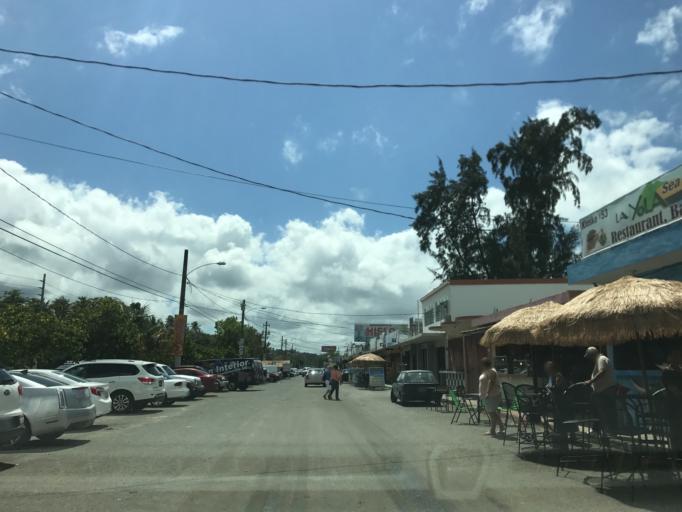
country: PR
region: Luquillo
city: Playa Fortuna
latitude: 18.3810
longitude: -65.7342
